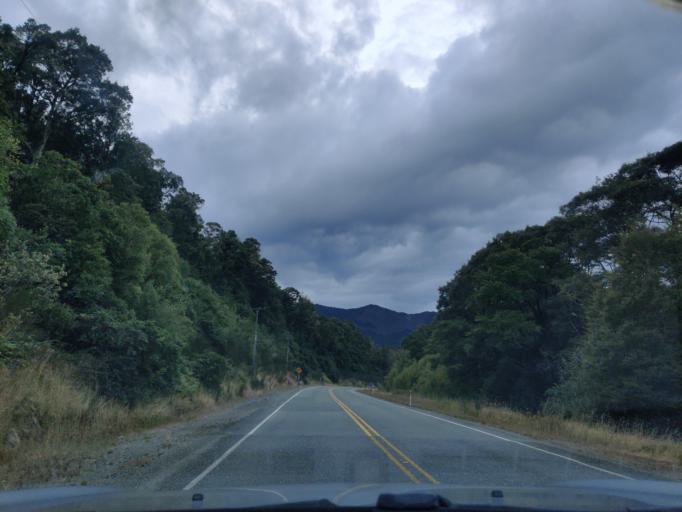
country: NZ
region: Tasman
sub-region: Tasman District
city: Wakefield
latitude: -41.6854
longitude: 172.4463
